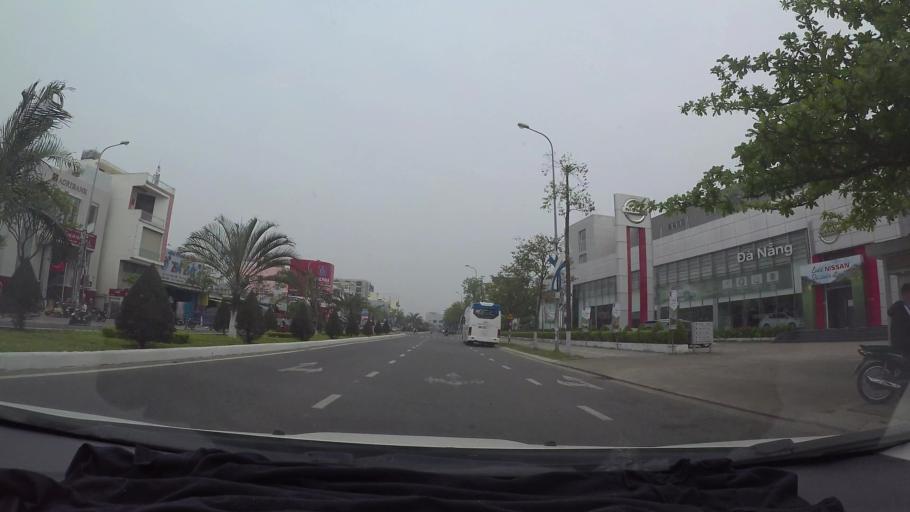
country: VN
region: Da Nang
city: Cam Le
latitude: 16.0214
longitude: 108.2107
